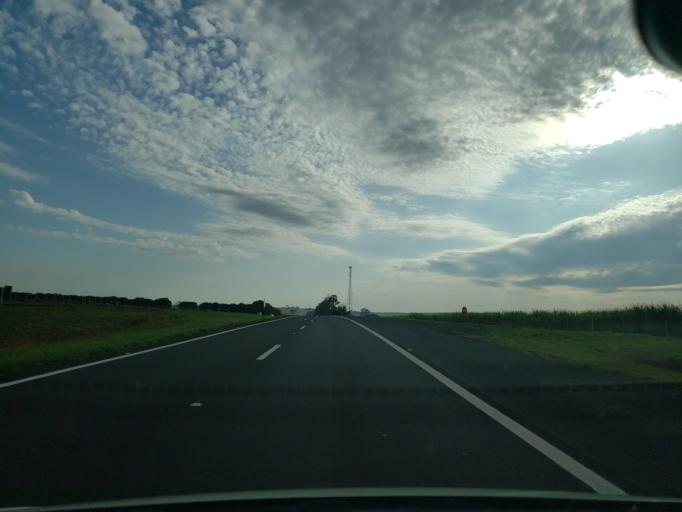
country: BR
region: Sao Paulo
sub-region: Valparaiso
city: Valparaiso
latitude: -21.2069
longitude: -50.7594
